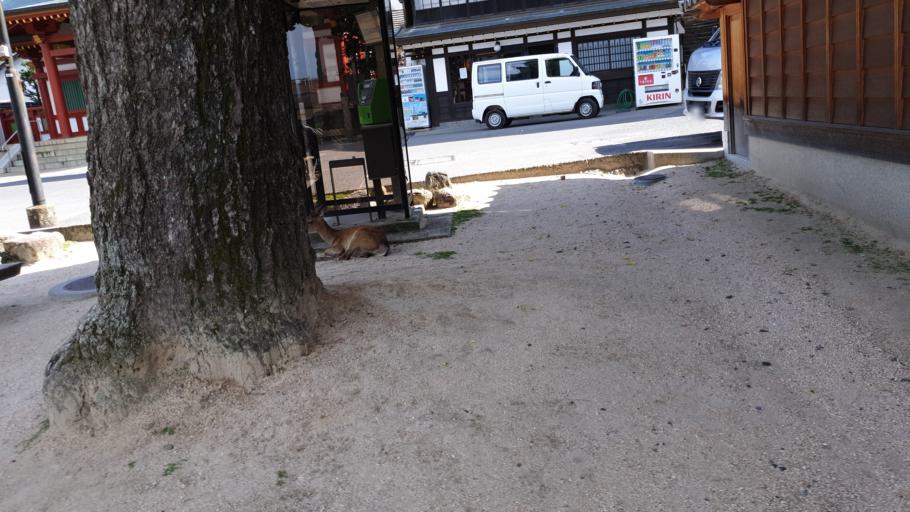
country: JP
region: Hiroshima
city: Miyajima
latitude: 34.2952
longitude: 132.3185
